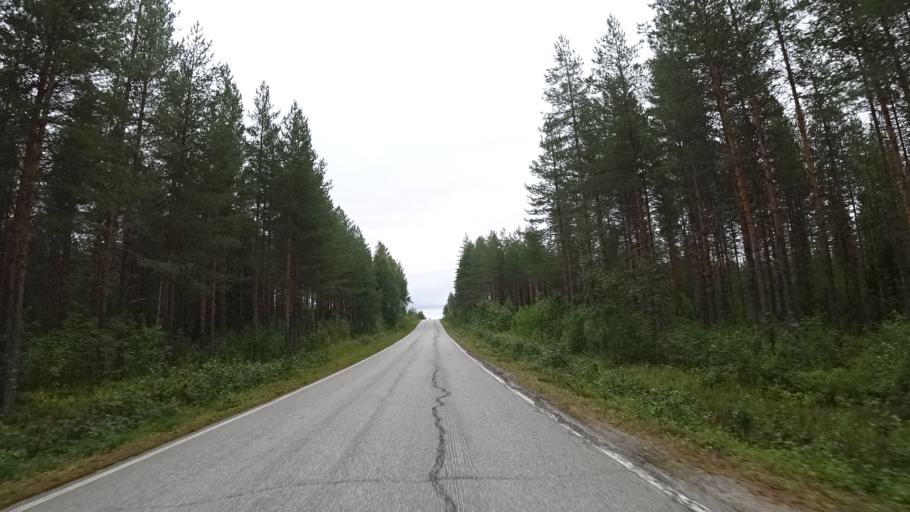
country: FI
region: North Karelia
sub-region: Pielisen Karjala
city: Lieksa
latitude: 63.3650
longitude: 30.2880
